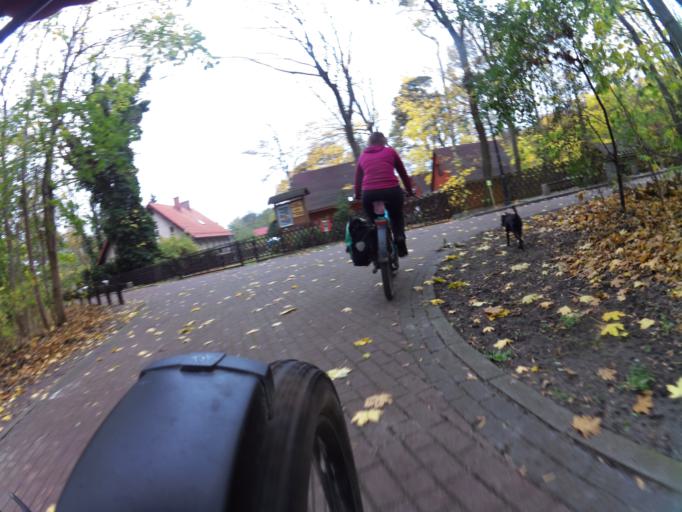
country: PL
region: Pomeranian Voivodeship
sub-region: Powiat pucki
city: Jastarnia
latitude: 54.6978
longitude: 18.6865
